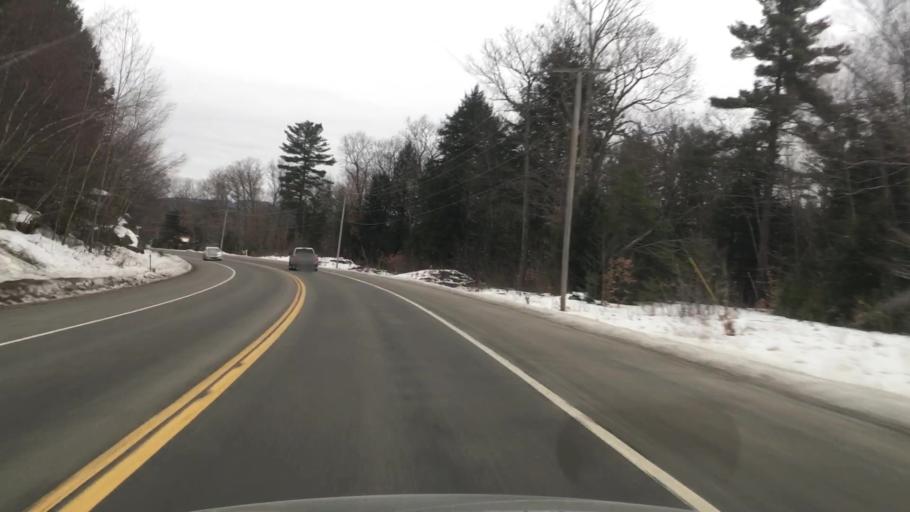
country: US
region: New Hampshire
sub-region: Merrimack County
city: Sutton
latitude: 43.2818
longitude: -71.9753
